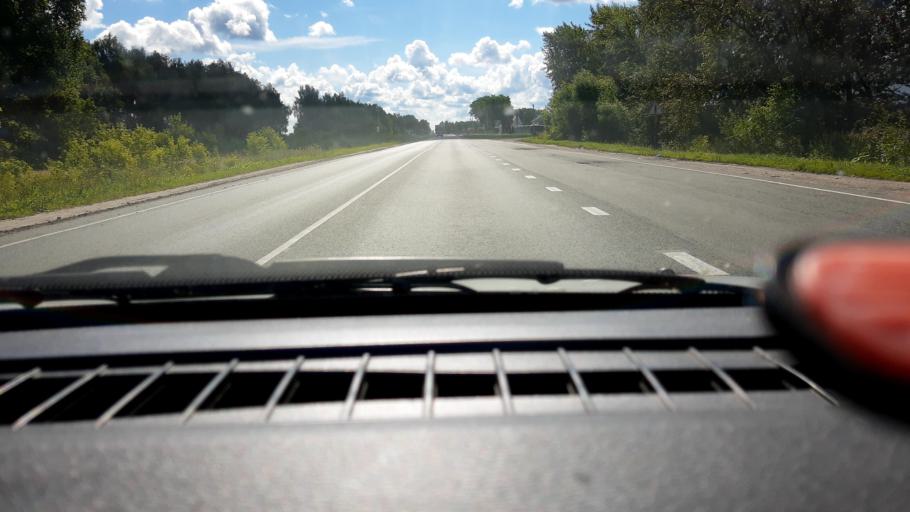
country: RU
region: Nizjnij Novgorod
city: Arzamas
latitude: 55.3005
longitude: 43.9277
